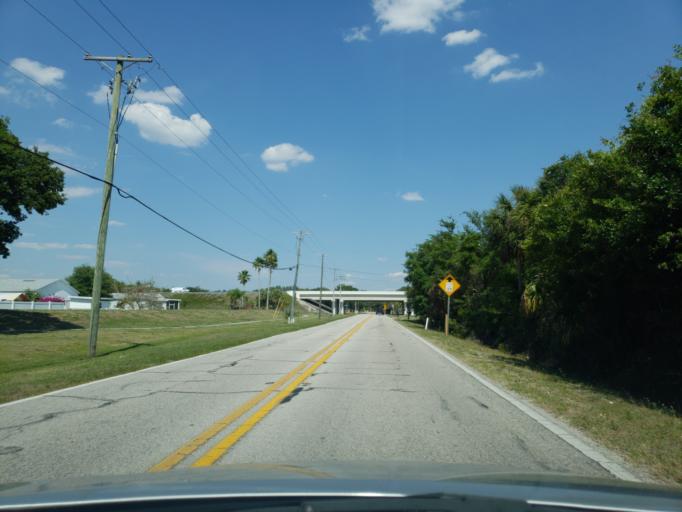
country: US
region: Florida
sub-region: Hillsborough County
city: Riverview
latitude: 27.8643
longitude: -82.3493
